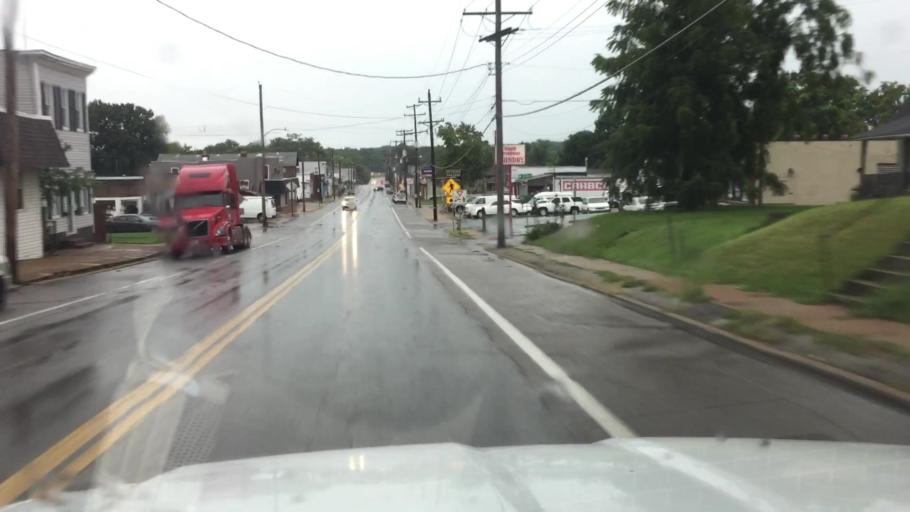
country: US
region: Missouri
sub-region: Saint Louis County
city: Lemay
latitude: 38.5311
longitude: -90.2771
